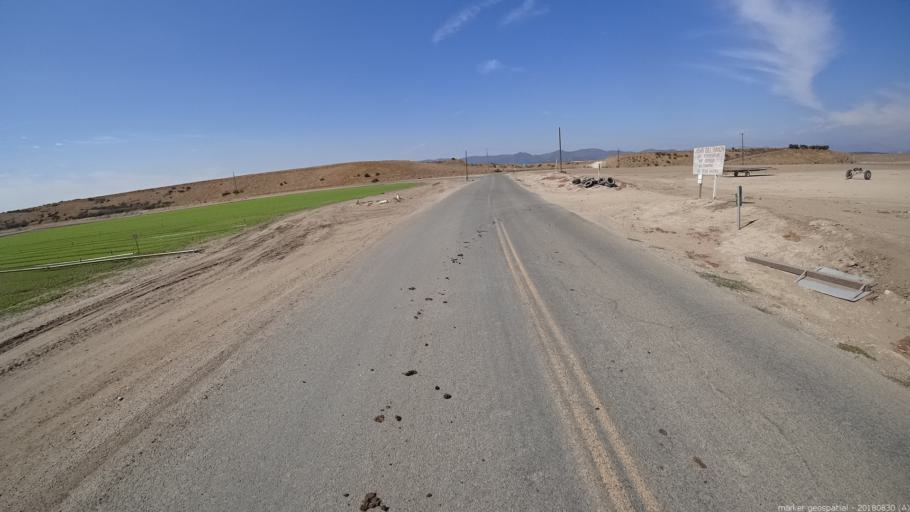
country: US
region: California
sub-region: Monterey County
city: King City
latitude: 36.1116
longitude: -121.0316
